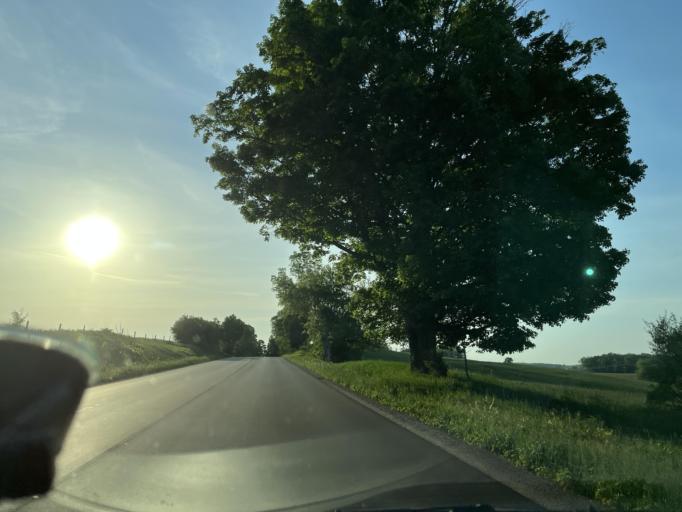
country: US
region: Michigan
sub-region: Barry County
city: Middleville
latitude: 42.7111
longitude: -85.4356
